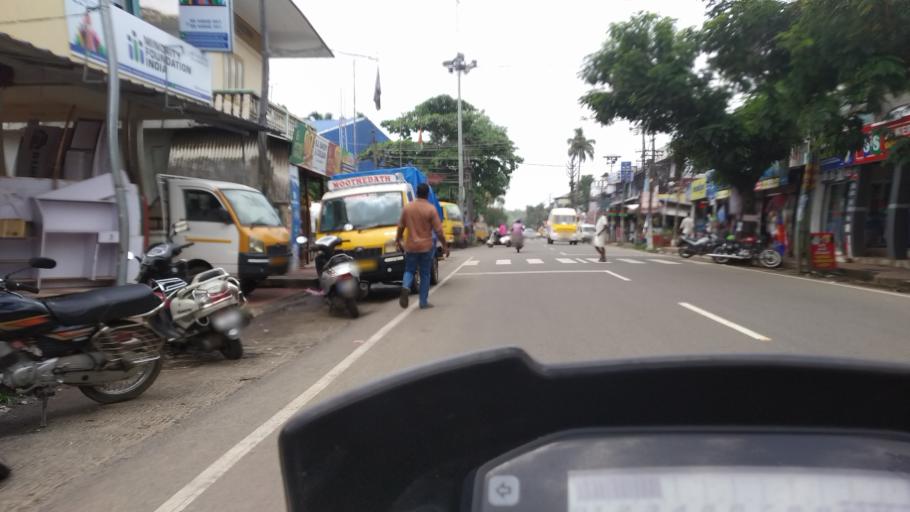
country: IN
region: Kerala
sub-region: Ernakulam
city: Aluva
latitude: 10.1276
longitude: 76.3086
